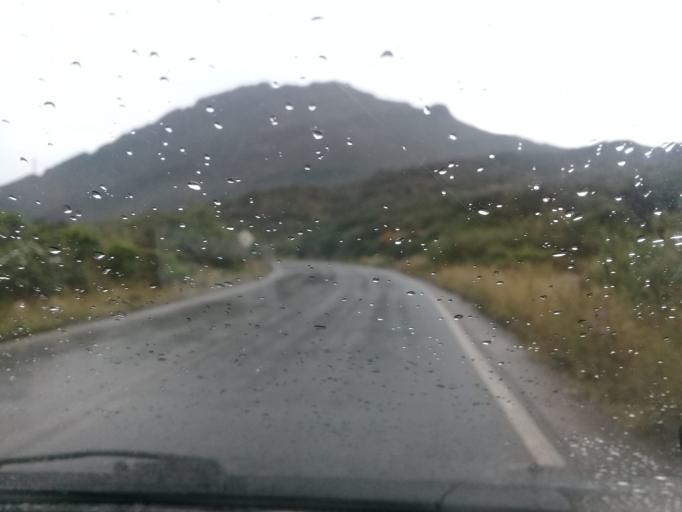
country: CO
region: Cundinamarca
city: Guasca
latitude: 4.8403
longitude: -73.8108
